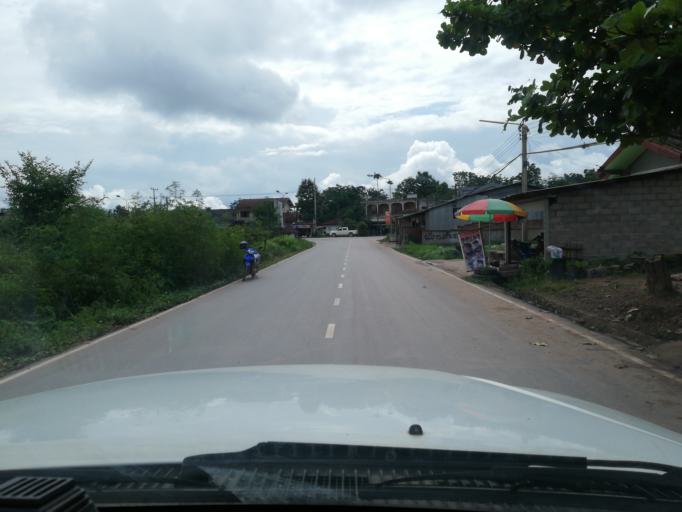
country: LA
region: Loungnamtha
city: Louang Namtha
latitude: 20.9515
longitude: 101.4024
